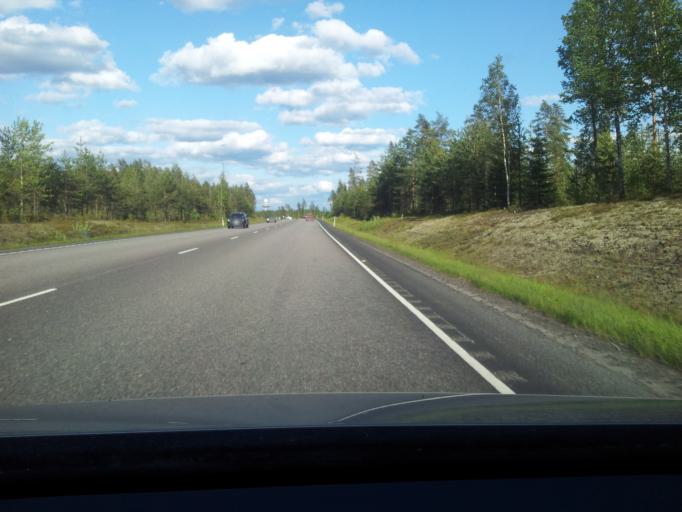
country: FI
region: Kymenlaakso
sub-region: Kouvola
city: Anjala
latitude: 60.9052
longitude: 27.0863
